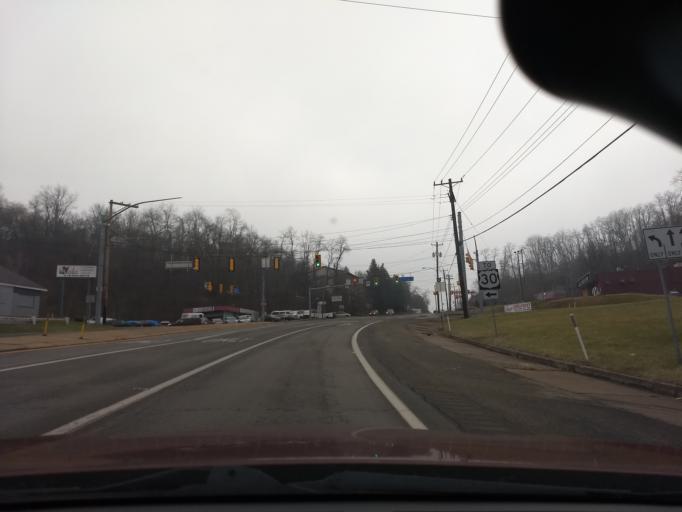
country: US
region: Pennsylvania
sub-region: Allegheny County
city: East Pittsburgh
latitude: 40.3838
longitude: -79.8278
